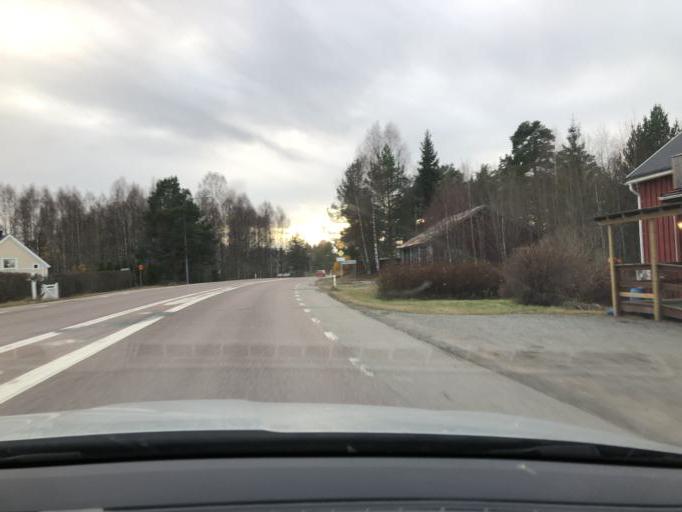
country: SE
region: Gaevleborg
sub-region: Hudiksvalls Kommun
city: Iggesund
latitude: 61.6057
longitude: 17.0544
